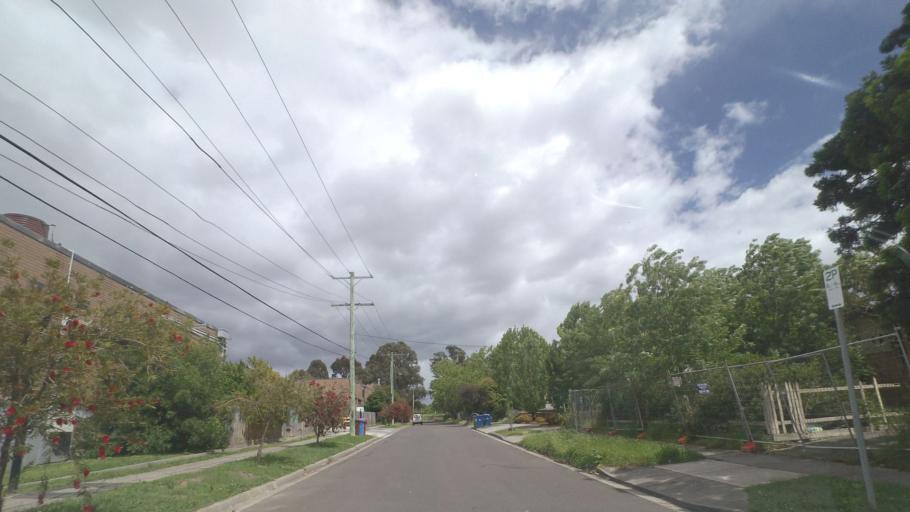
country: AU
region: Victoria
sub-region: Knox
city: Boronia
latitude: -37.8609
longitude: 145.2824
